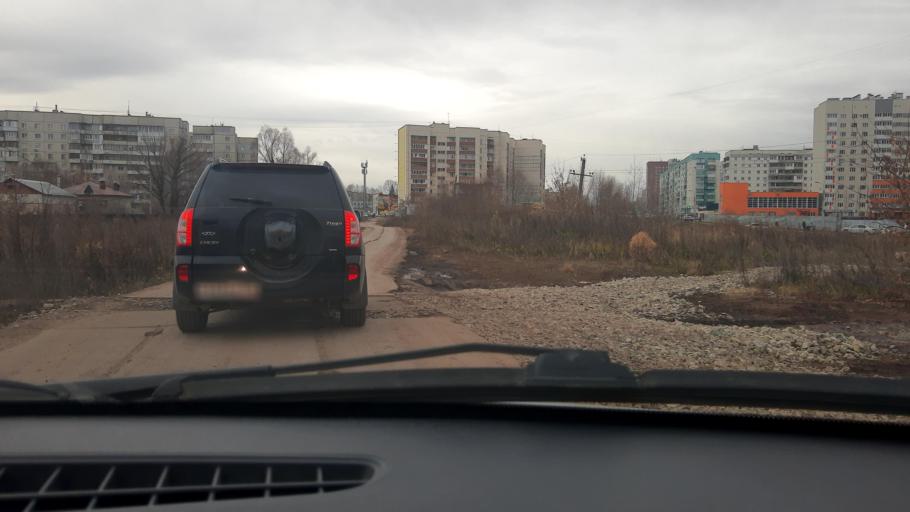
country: RU
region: Bashkortostan
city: Mikhaylovka
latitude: 54.7111
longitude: 55.8396
